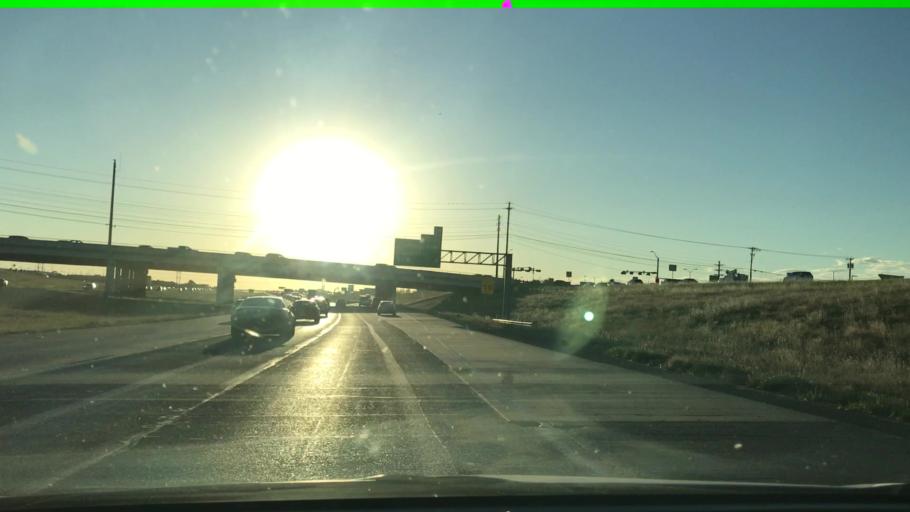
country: US
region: Texas
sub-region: Dallas County
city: Coppell
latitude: 32.9237
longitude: -96.9956
